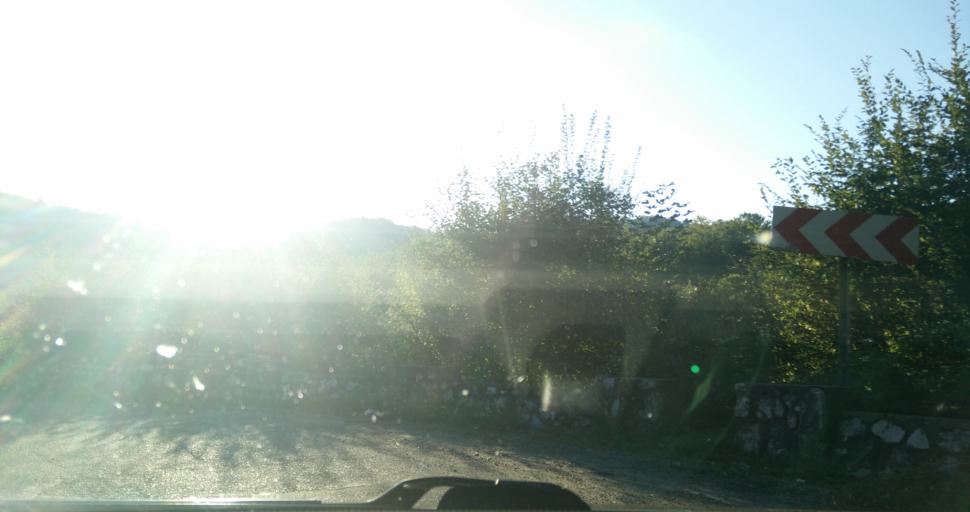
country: RO
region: Bihor
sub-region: Oras Nucet
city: Nucet
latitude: 46.4881
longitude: 22.6048
